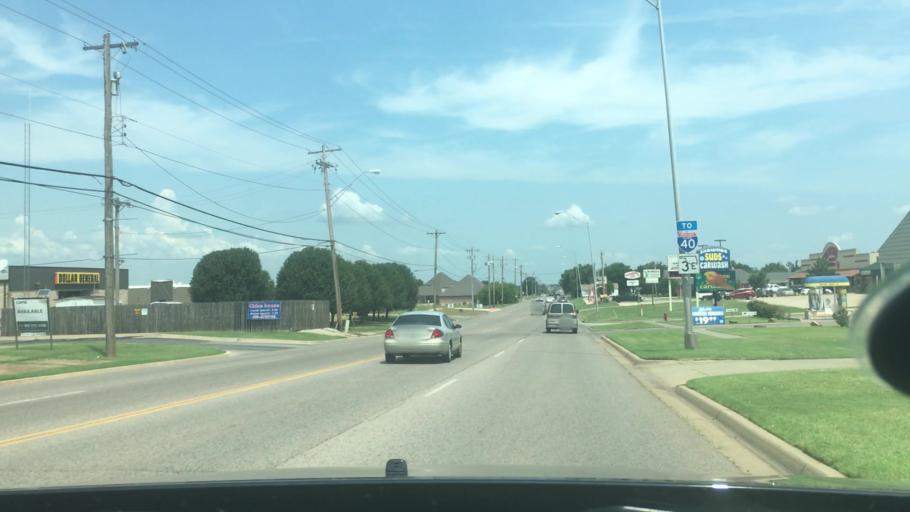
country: US
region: Oklahoma
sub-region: Pottawatomie County
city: Shawnee
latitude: 35.3629
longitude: -96.9298
